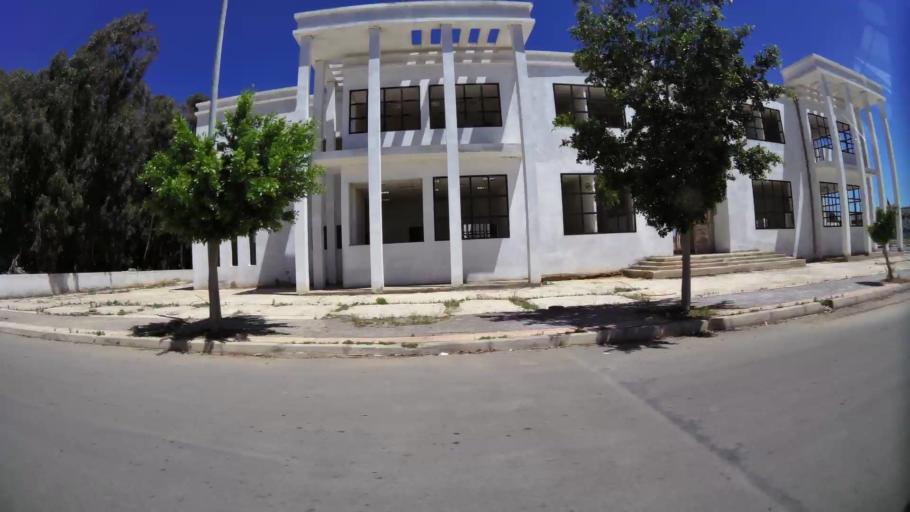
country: MA
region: Oriental
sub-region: Berkane-Taourirt
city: Madagh
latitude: 35.0877
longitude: -2.2415
